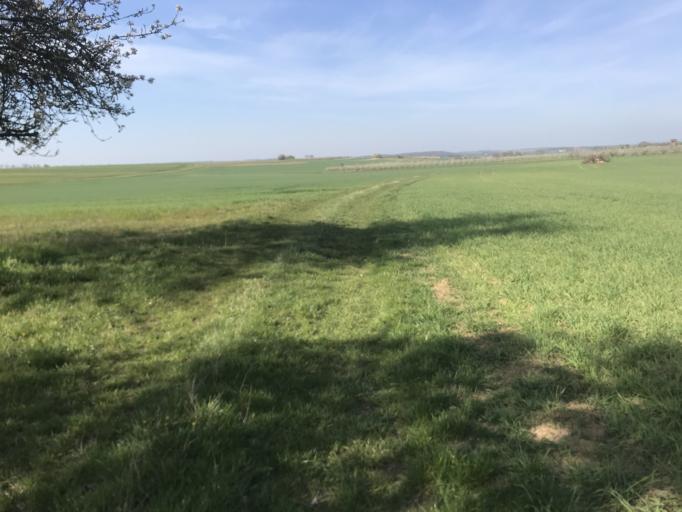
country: DE
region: Rheinland-Pfalz
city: Wackernheim
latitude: 49.9531
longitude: 8.1132
